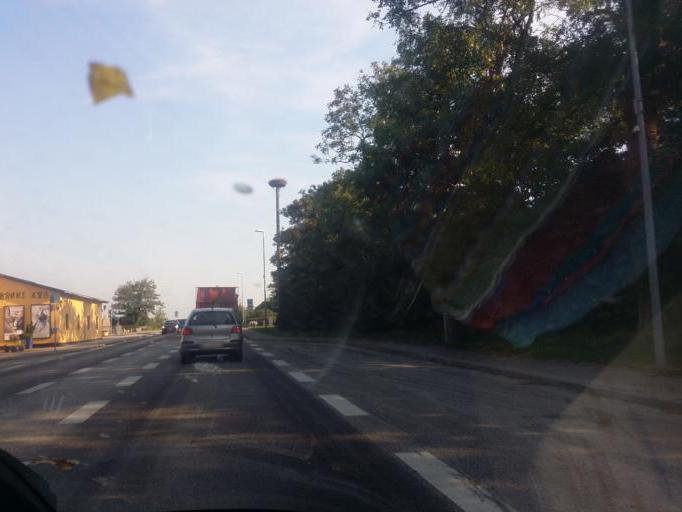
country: DK
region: South Denmark
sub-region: Tonder Kommune
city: Sherrebek
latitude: 55.1942
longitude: 8.7273
